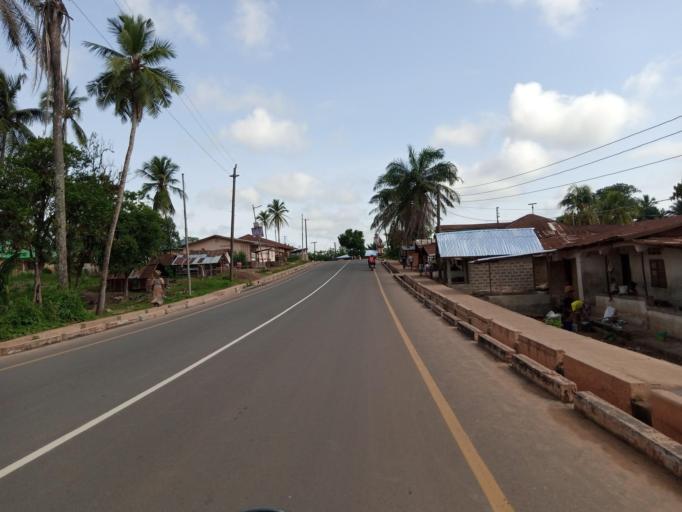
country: SL
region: Southern Province
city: Bo
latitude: 7.9554
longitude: -11.7204
